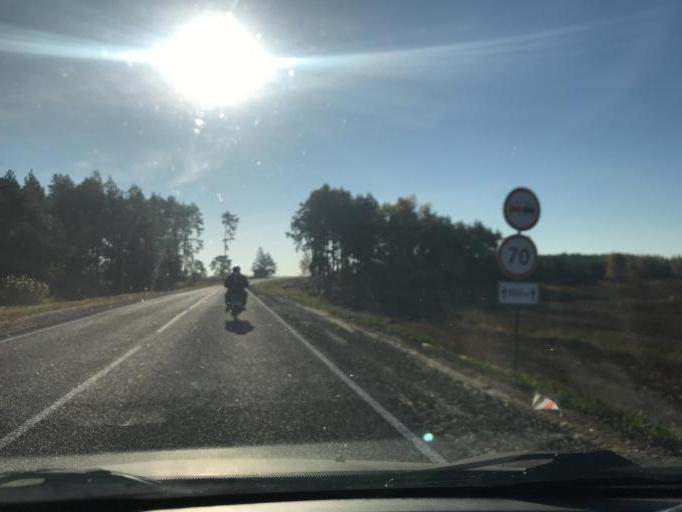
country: BY
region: Gomel
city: Brahin
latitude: 51.7693
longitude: 30.2993
